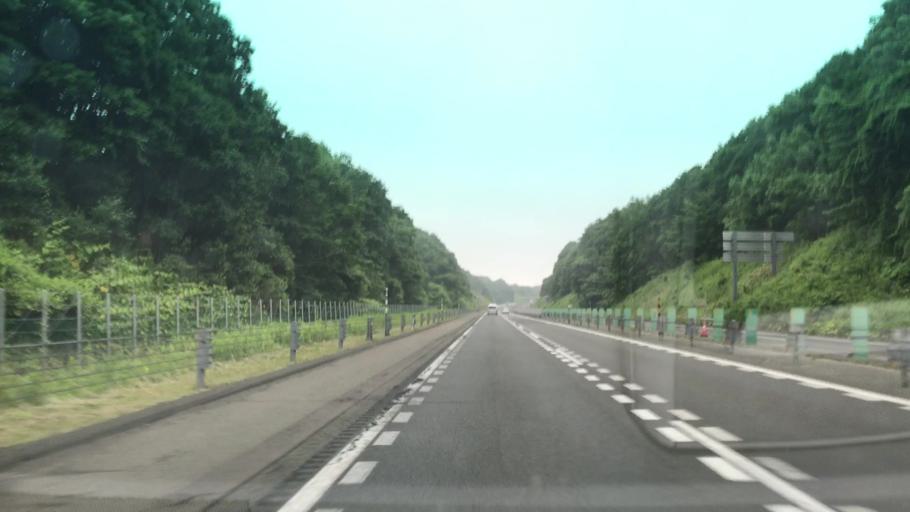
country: JP
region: Hokkaido
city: Kitahiroshima
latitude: 42.9291
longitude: 141.5345
